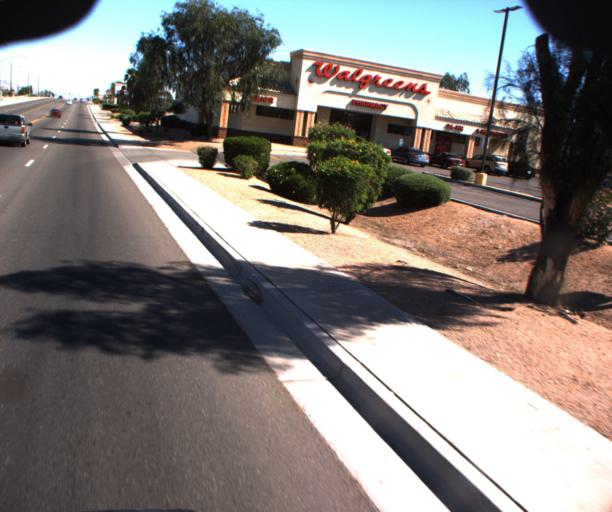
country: US
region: Arizona
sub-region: Mohave County
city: Bullhead City
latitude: 35.1008
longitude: -114.5979
